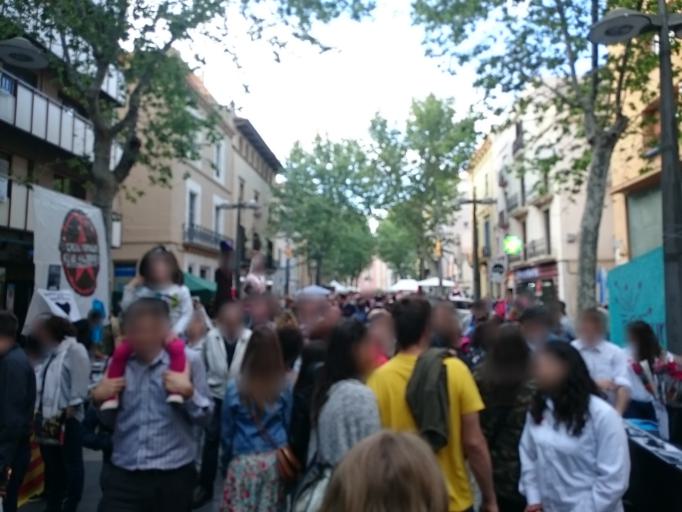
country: ES
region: Catalonia
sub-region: Provincia de Barcelona
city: Vilanova i la Geltru
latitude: 41.2251
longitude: 1.7243
